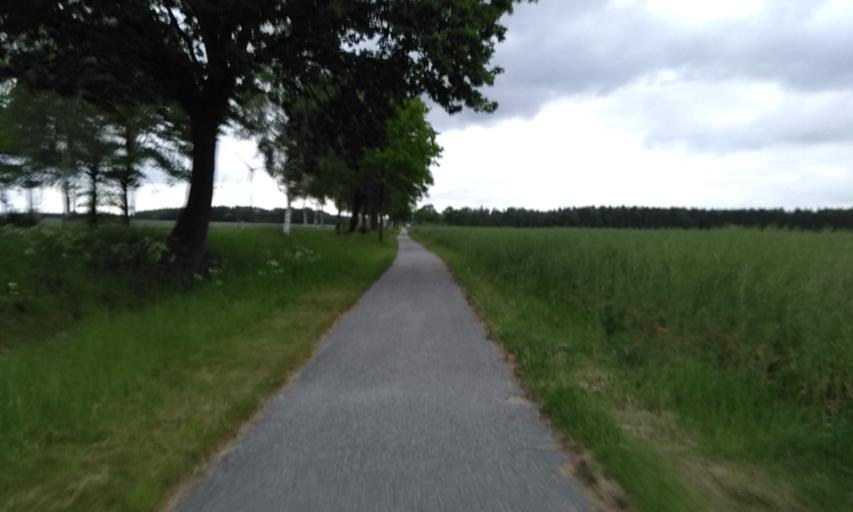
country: DE
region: Lower Saxony
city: Harsefeld
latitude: 53.4803
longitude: 9.4933
